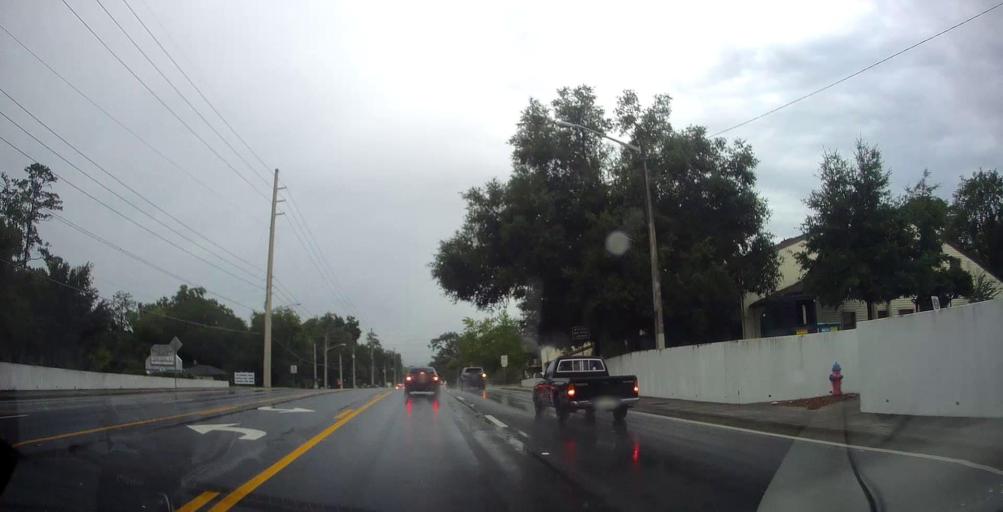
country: US
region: Florida
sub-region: Marion County
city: Ocala
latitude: 29.1874
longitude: -82.0869
